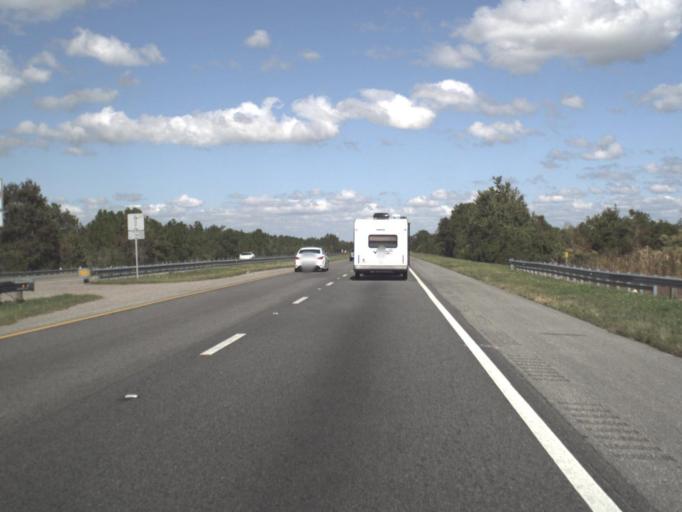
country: US
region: Florida
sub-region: Osceola County
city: Saint Cloud
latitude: 28.1275
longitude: -81.2880
